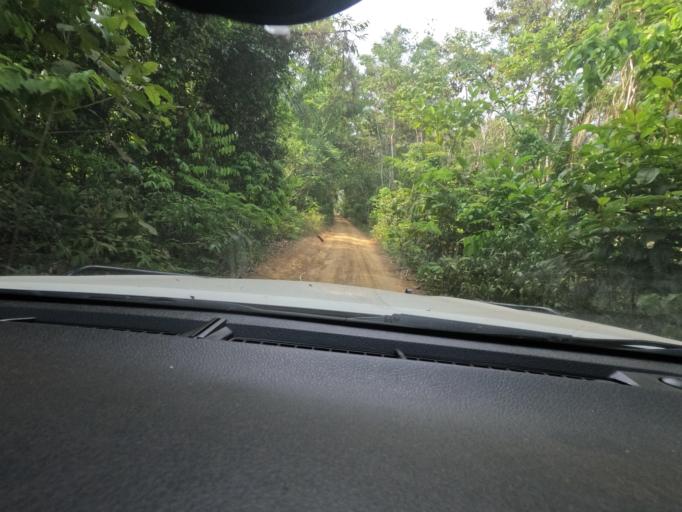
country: BR
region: Rondonia
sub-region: Porto Velho
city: Porto Velho
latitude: -8.6641
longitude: -63.1560
